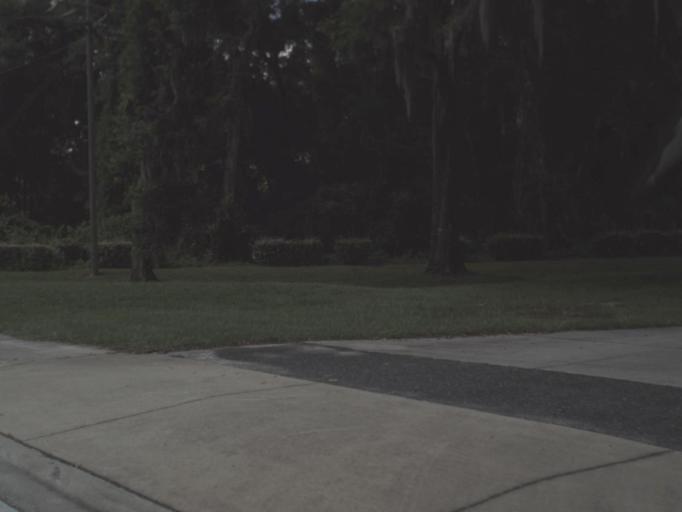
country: US
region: Florida
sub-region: Citrus County
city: Inverness Highlands South
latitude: 28.8006
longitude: -82.3089
